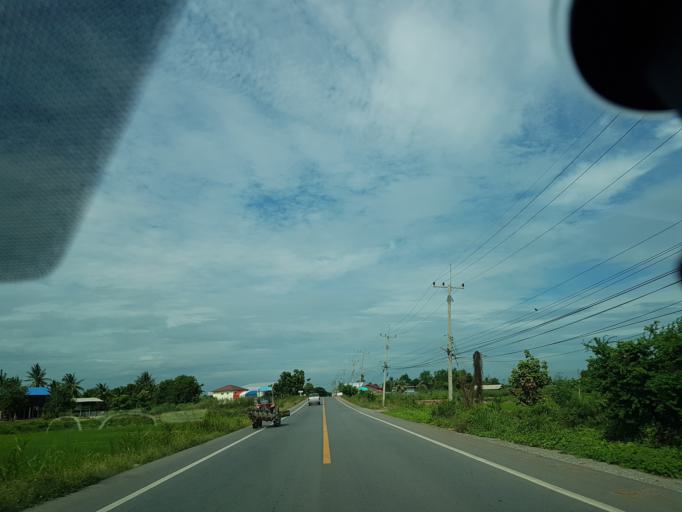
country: TH
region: Lop Buri
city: Tha Wung
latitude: 14.7537
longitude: 100.5551
